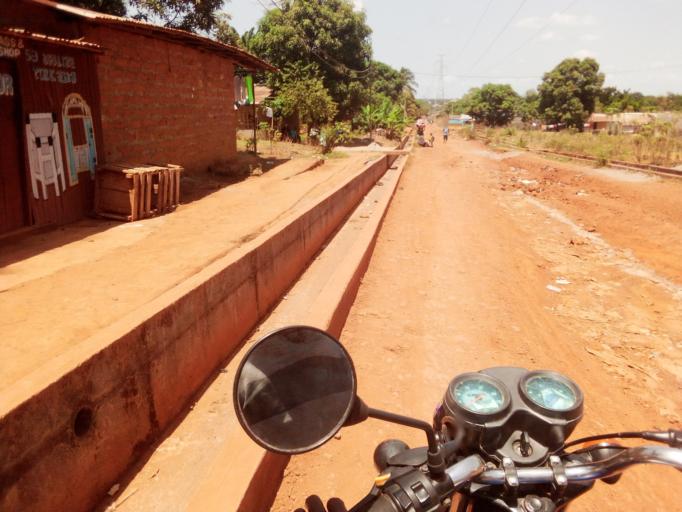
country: SL
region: Western Area
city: Waterloo
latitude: 8.3303
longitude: -13.0777
